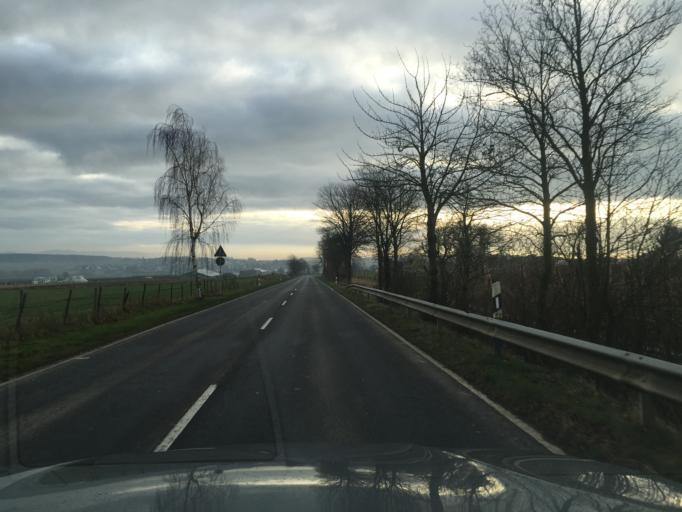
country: DE
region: North Rhine-Westphalia
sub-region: Regierungsbezirk Koln
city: Wachtberg
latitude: 50.6143
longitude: 7.1354
